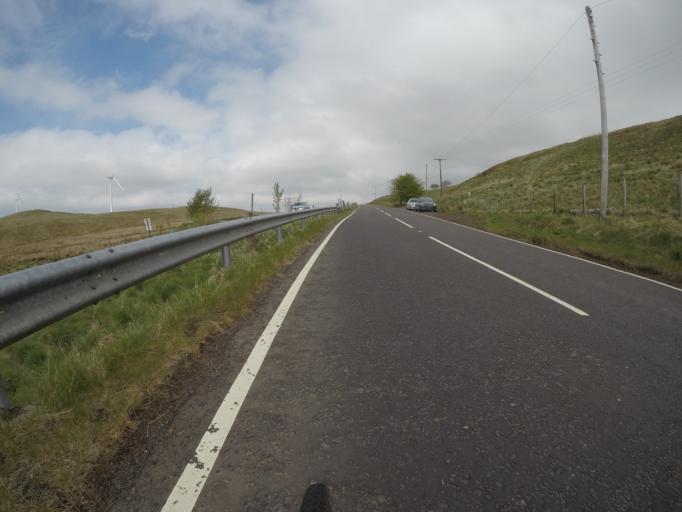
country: GB
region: Scotland
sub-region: East Renfrewshire
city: Neilston
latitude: 55.7411
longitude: -4.4055
